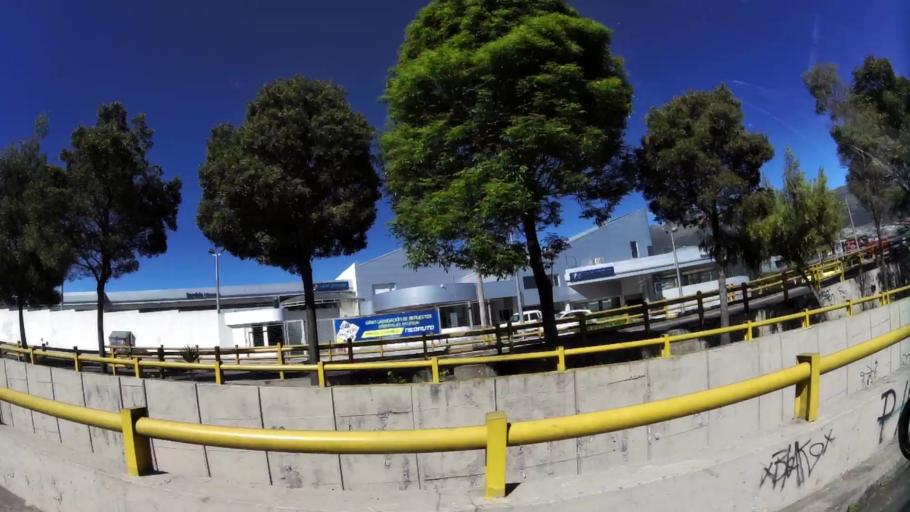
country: EC
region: Pichincha
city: Quito
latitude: -0.1215
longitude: -78.4796
